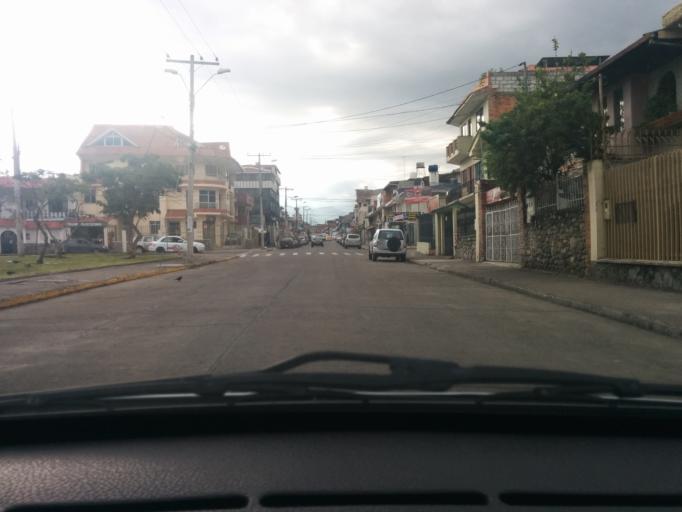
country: EC
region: Azuay
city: Cuenca
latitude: -2.8996
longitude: -78.9921
